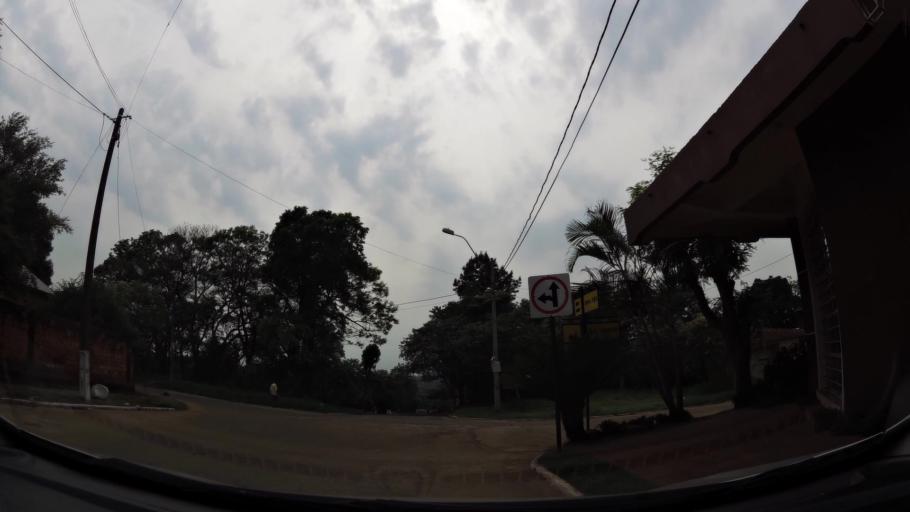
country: BR
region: Parana
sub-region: Foz Do Iguacu
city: Foz do Iguacu
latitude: -25.5604
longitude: -54.6041
